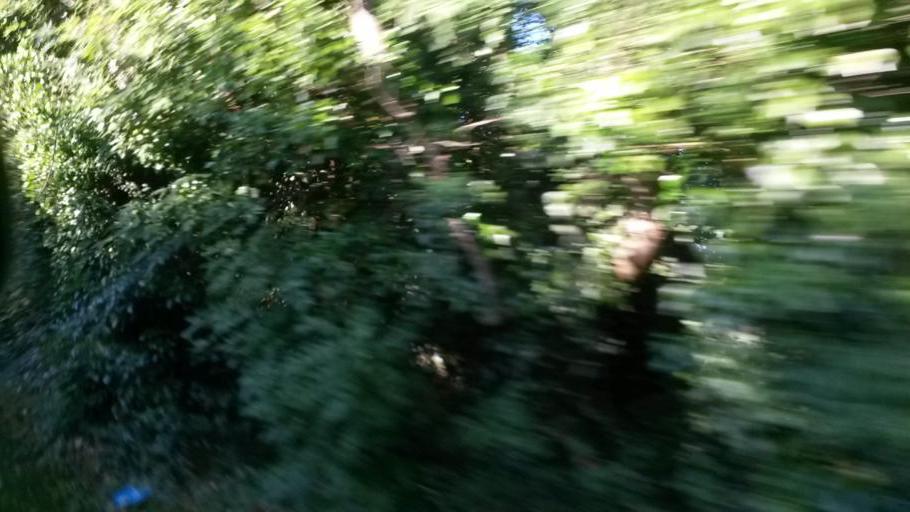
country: IE
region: Leinster
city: Ballymun
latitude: 53.4536
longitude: -6.2944
